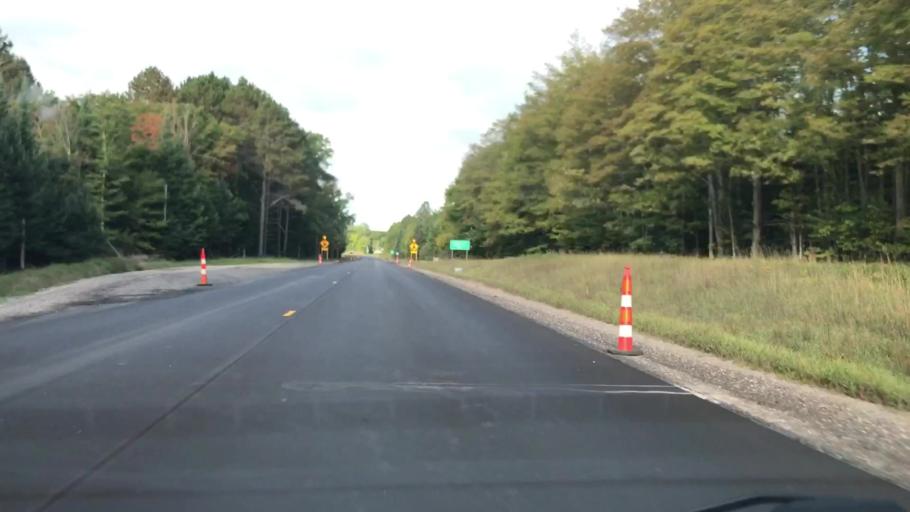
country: US
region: Michigan
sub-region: Luce County
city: Newberry
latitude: 46.3464
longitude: -85.0199
